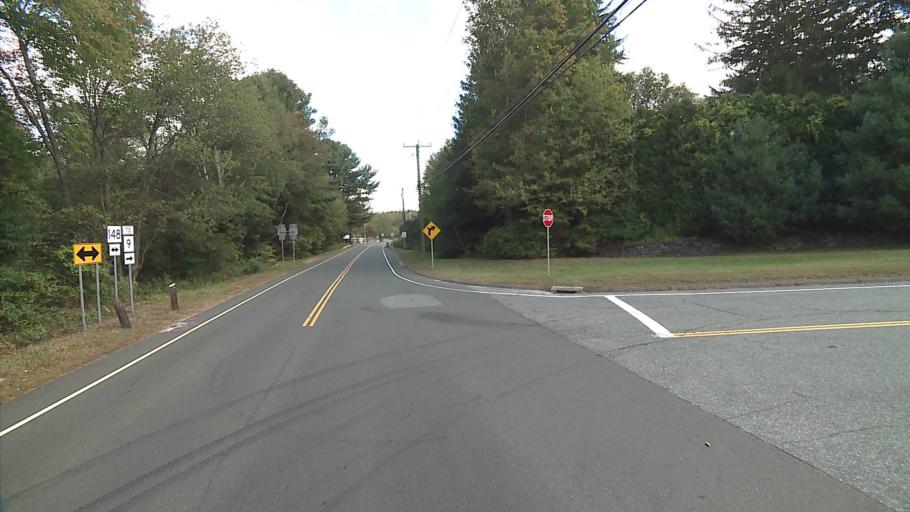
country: US
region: Connecticut
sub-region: Middlesex County
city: Chester Center
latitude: 41.3964
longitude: -72.5018
